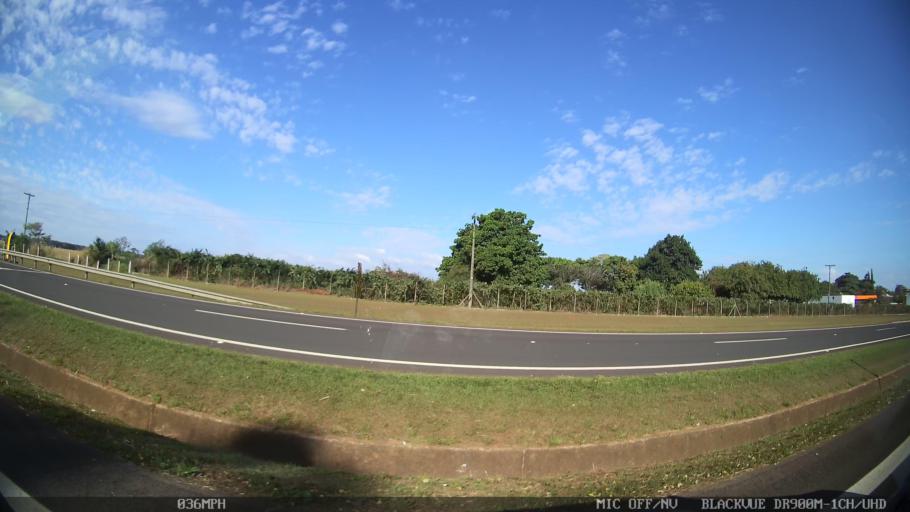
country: BR
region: Sao Paulo
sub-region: Iracemapolis
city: Iracemapolis
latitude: -22.6559
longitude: -47.5201
